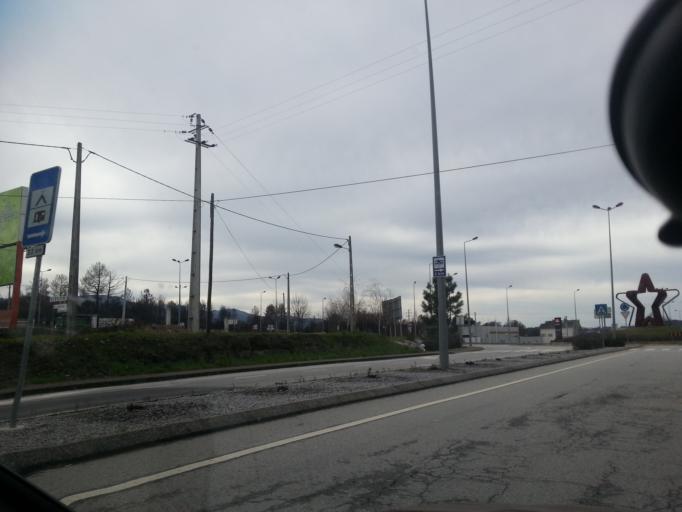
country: PT
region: Guarda
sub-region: Seia
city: Seia
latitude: 40.5128
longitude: -7.6314
